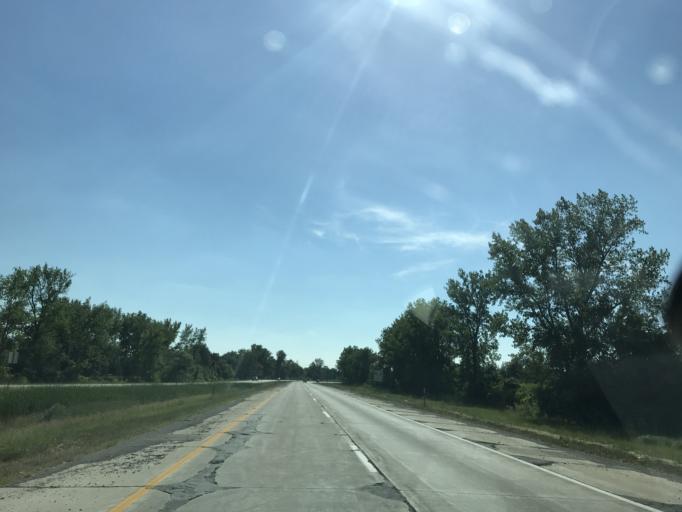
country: US
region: Michigan
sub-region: Bay County
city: Bay City
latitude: 43.5979
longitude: -83.9228
